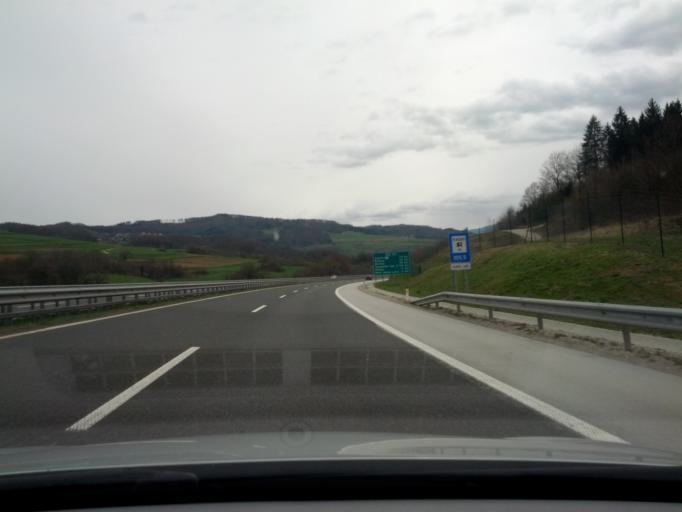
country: SI
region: Mirna Pec
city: Mirna Pec
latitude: 45.8734
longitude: 15.1060
